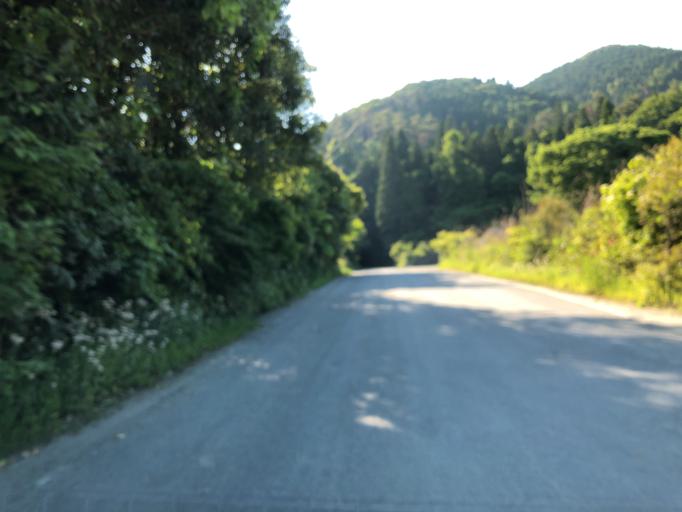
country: JP
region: Ibaraki
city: Kitaibaraki
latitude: 36.8648
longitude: 140.7125
